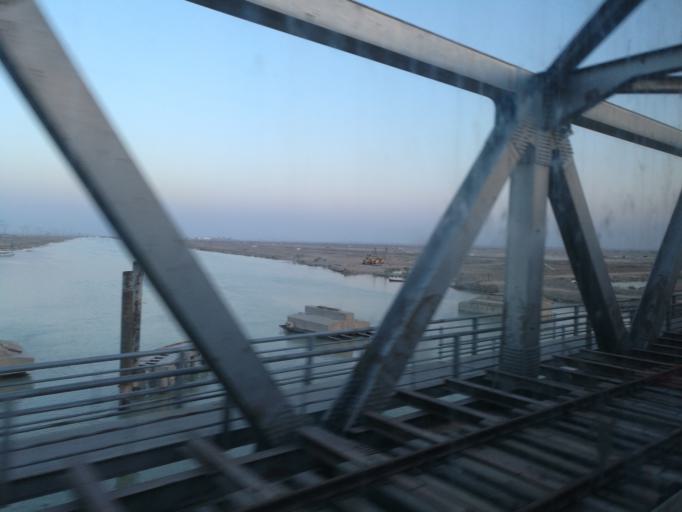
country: IQ
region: Basra Governorate
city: Al Harithah
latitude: 30.5204
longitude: 47.7220
